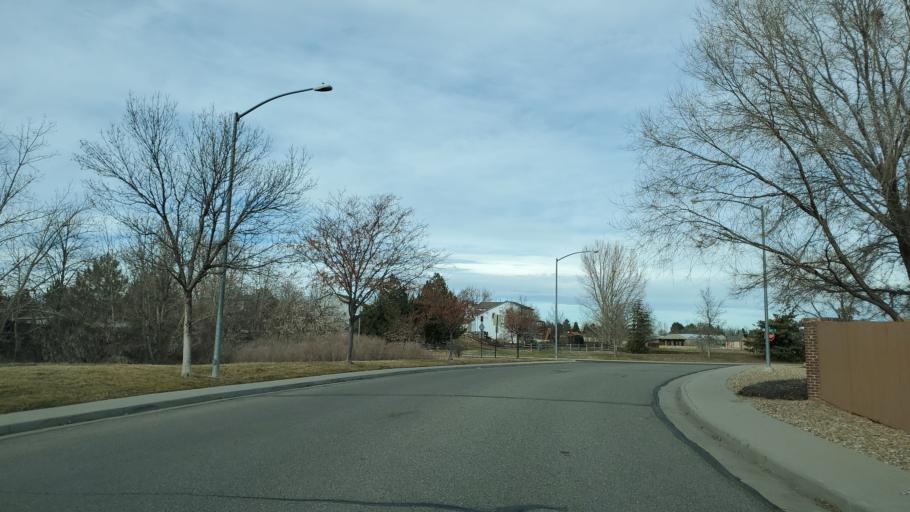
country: US
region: Colorado
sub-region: Adams County
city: Northglenn
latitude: 39.9164
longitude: -104.9494
